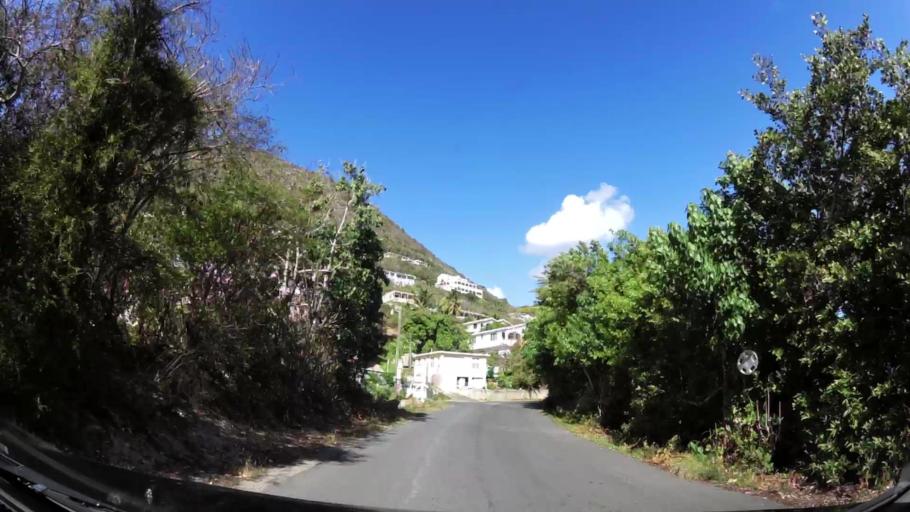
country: VG
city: Road Town
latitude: 18.3871
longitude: -64.6980
